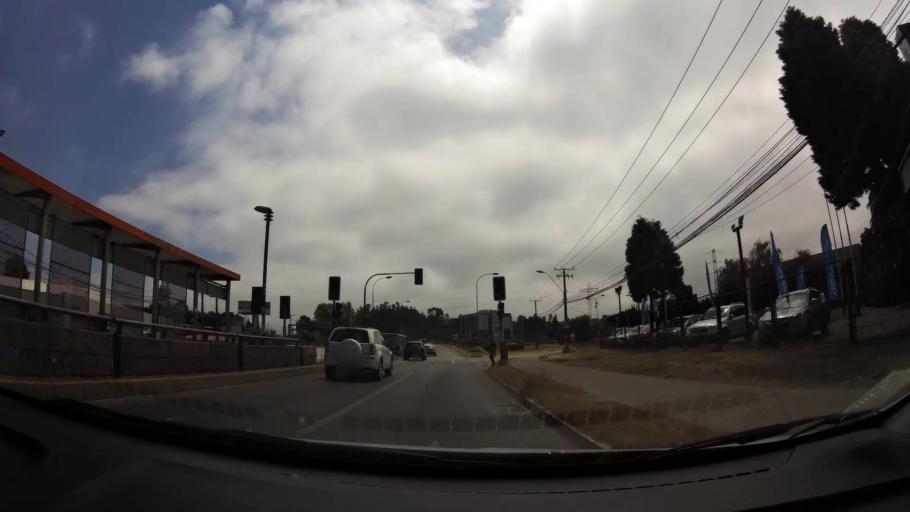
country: CL
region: Biobio
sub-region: Provincia de Concepcion
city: Concepcion
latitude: -36.8009
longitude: -73.0566
